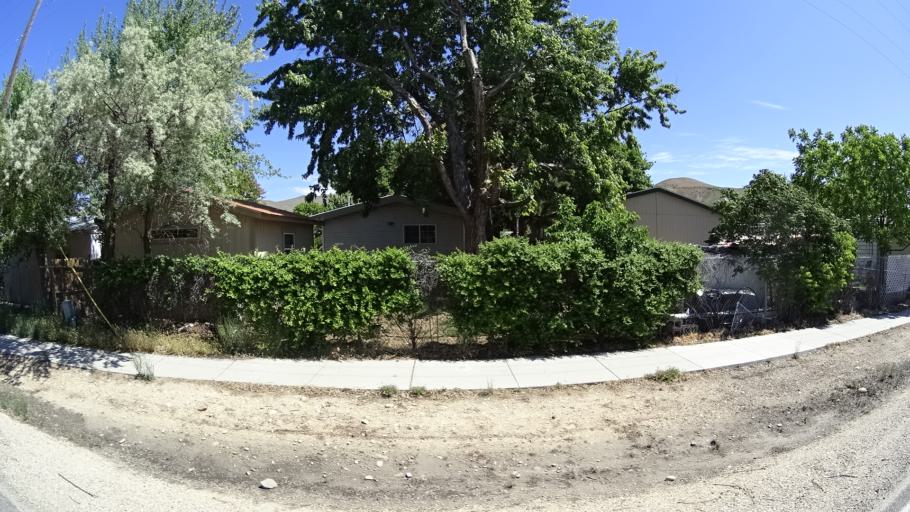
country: US
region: Idaho
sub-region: Ada County
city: Boise
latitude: 43.5673
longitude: -116.1175
